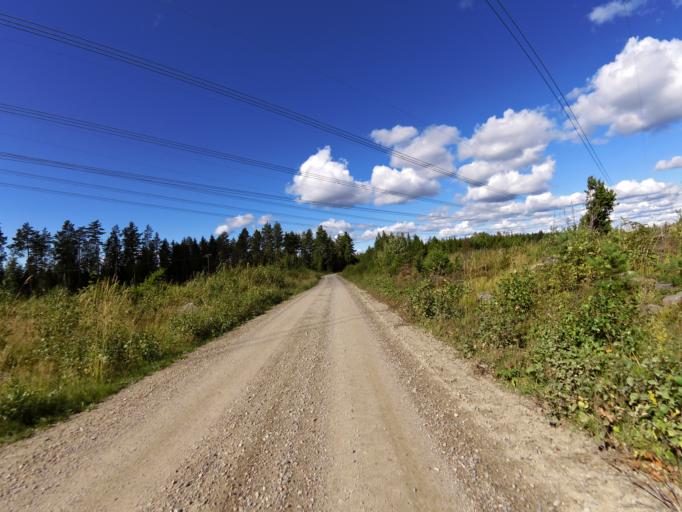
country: SE
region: Gaevleborg
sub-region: Gavle Kommun
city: Valbo
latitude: 60.7757
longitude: 16.9183
